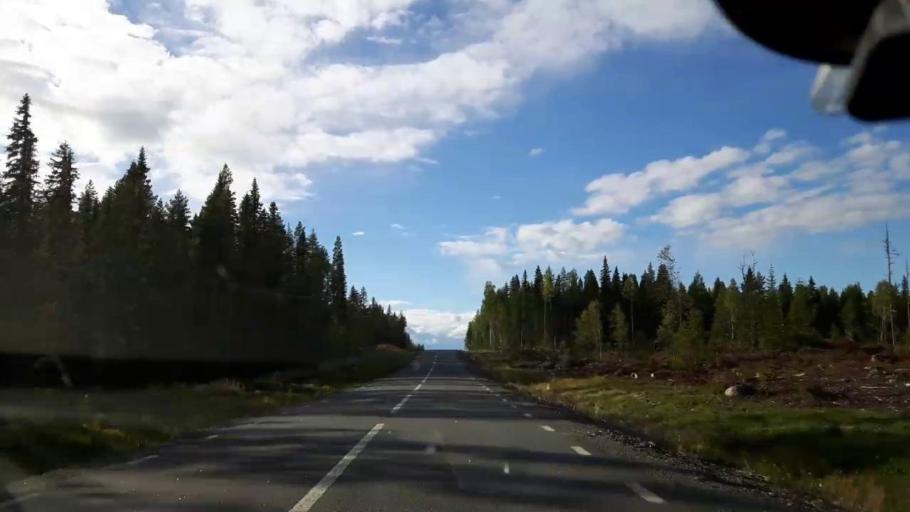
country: SE
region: Jaemtland
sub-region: Stroemsunds Kommun
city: Stroemsund
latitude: 63.5672
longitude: 15.7825
